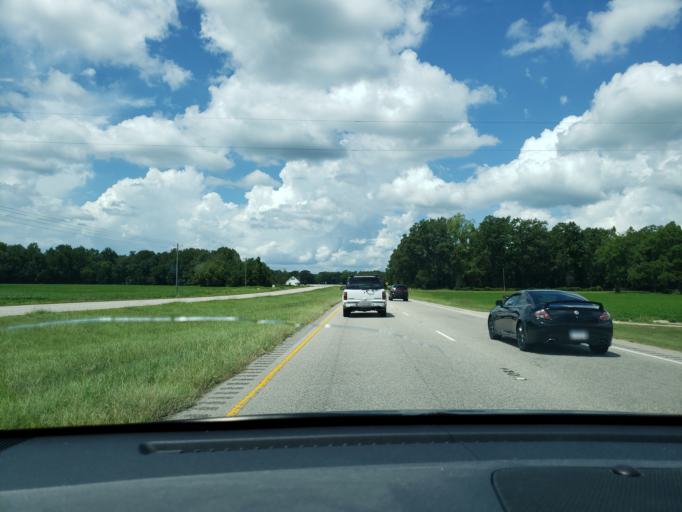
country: US
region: North Carolina
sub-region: Bladen County
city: Elizabethtown
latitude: 34.7180
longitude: -78.7540
